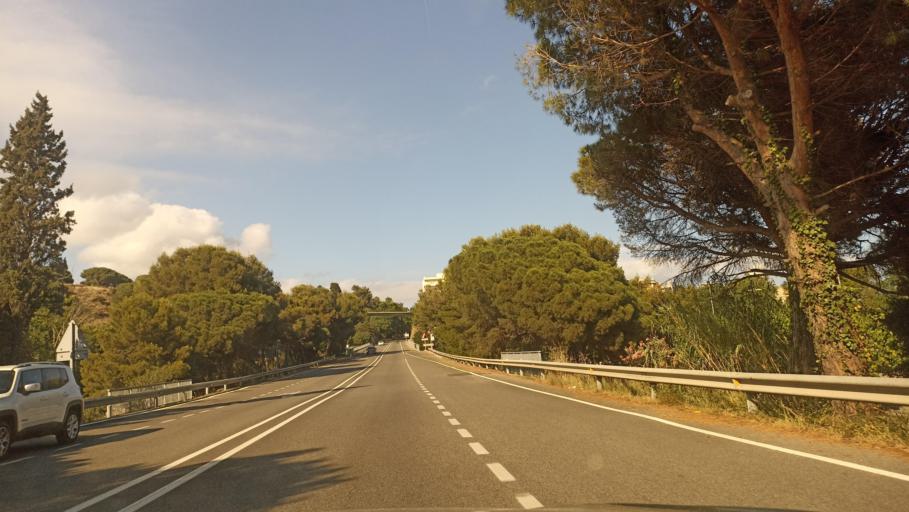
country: ES
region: Catalonia
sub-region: Provincia de Barcelona
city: Sant Pol de Mar
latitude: 41.5997
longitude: 2.6163
